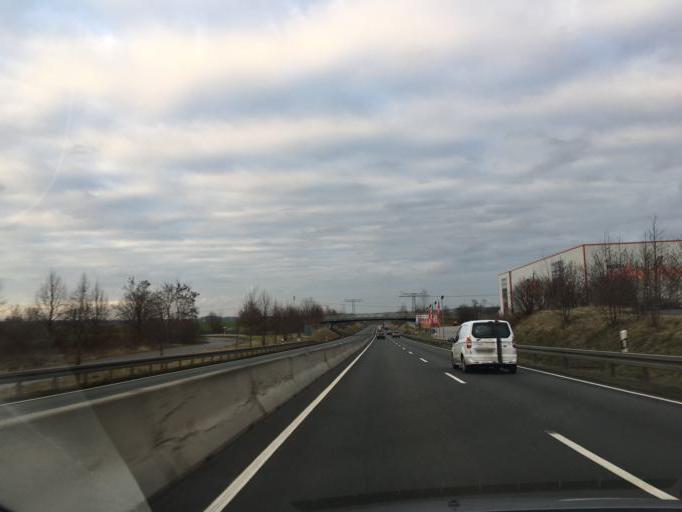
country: DE
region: Thuringia
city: Gerstenberg
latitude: 51.0146
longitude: 12.4541
